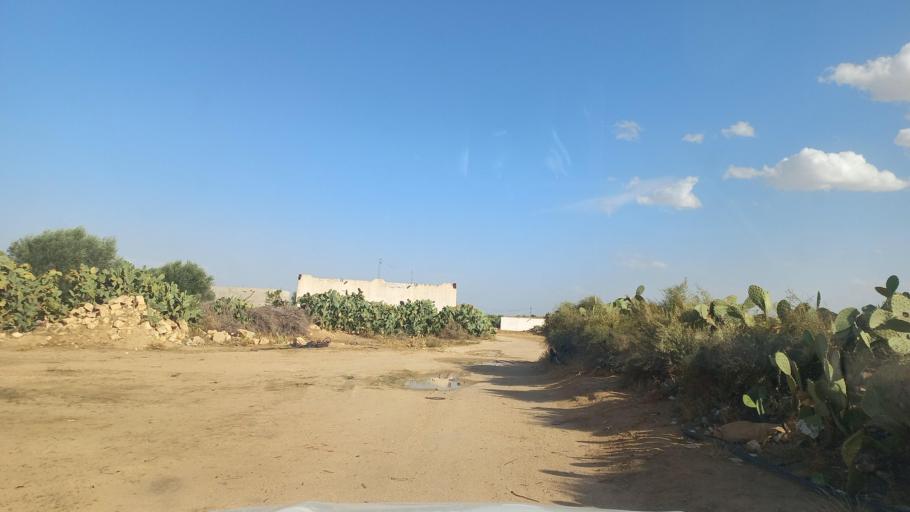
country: TN
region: Al Qasrayn
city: Kasserine
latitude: 35.2572
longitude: 9.0298
